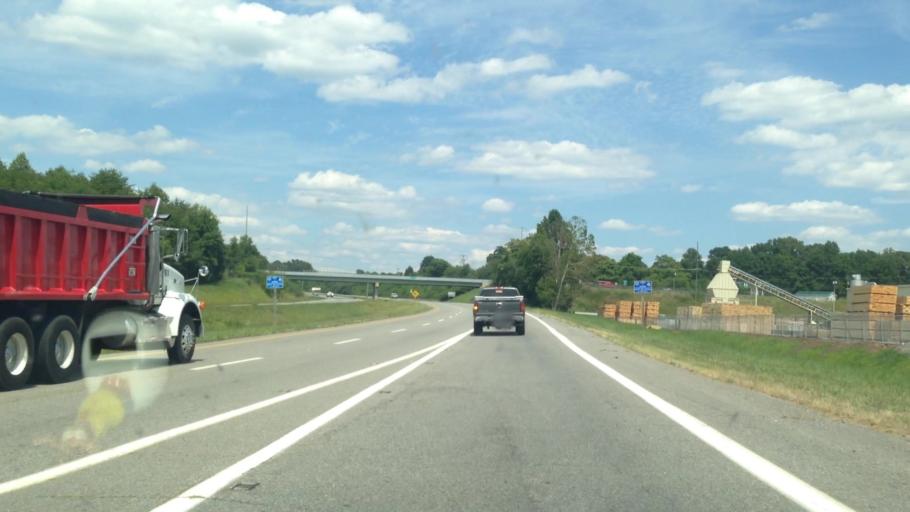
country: US
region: Virginia
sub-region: Henry County
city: Chatmoss
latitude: 36.6227
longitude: -79.8553
